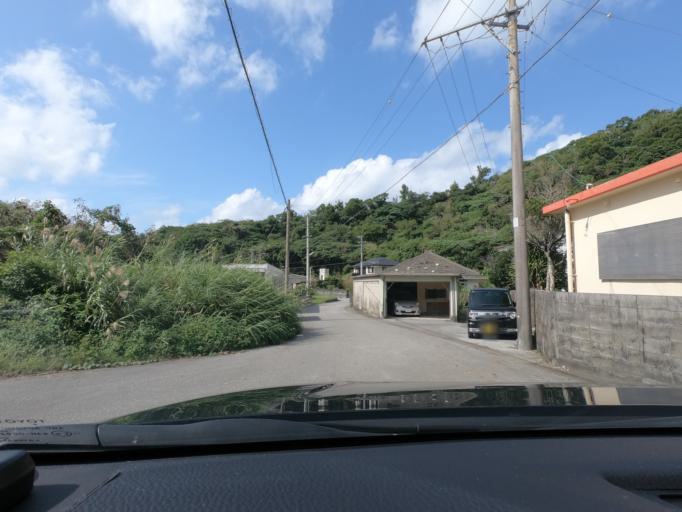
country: JP
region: Okinawa
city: Nago
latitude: 26.7575
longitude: 128.1913
